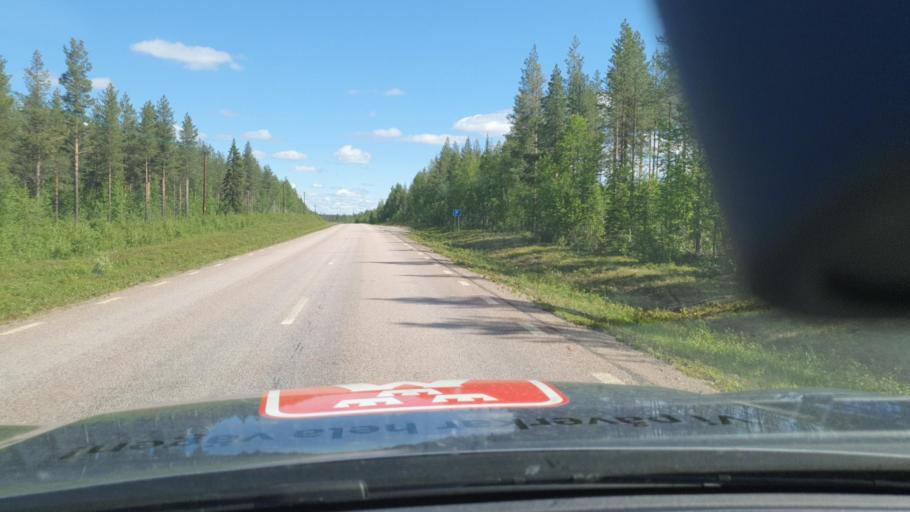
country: SE
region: Norrbotten
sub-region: Pajala Kommun
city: Pajala
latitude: 67.0959
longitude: 22.5765
